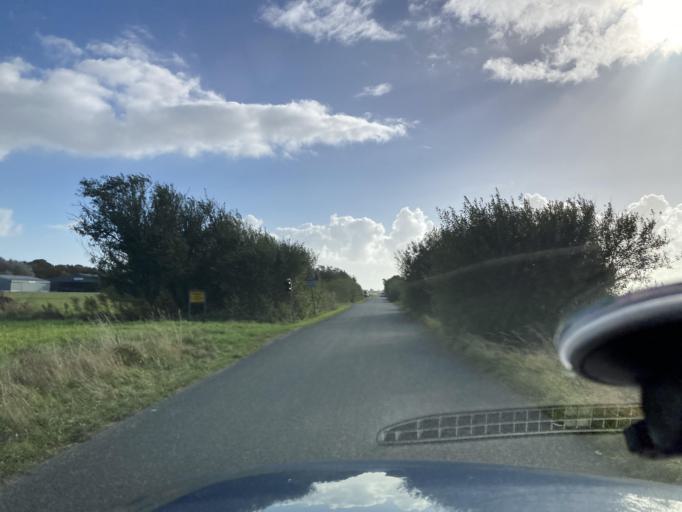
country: DE
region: Schleswig-Holstein
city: Oesterdeichstrich
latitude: 54.1554
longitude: 8.8953
